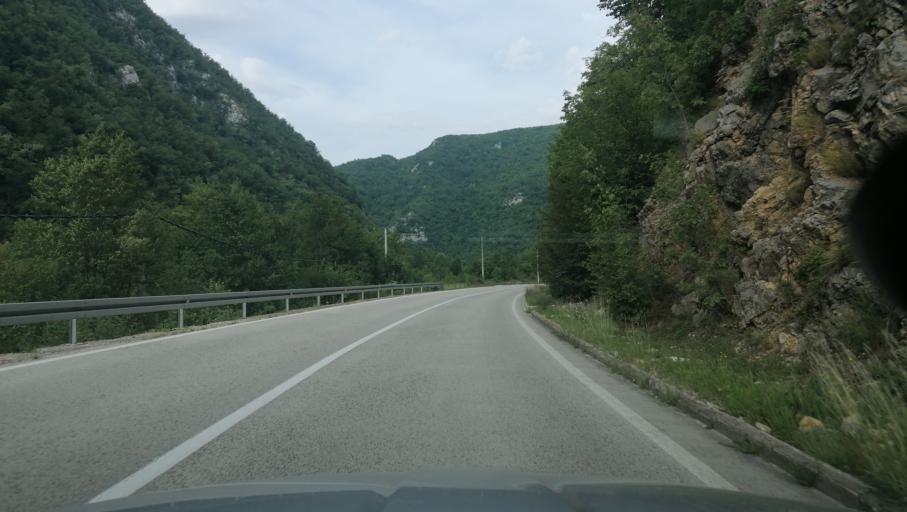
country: BA
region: Republika Srpska
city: Mrkonjic Grad
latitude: 44.4645
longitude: 17.2087
